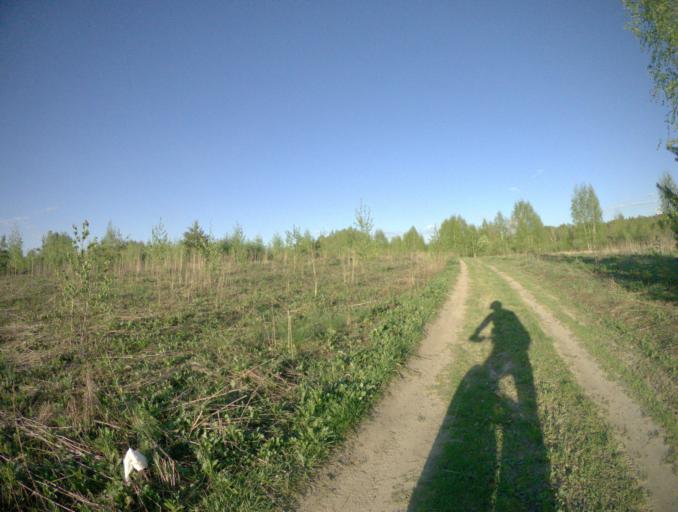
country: RU
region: Vladimir
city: Raduzhnyy
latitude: 55.9946
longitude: 40.2353
